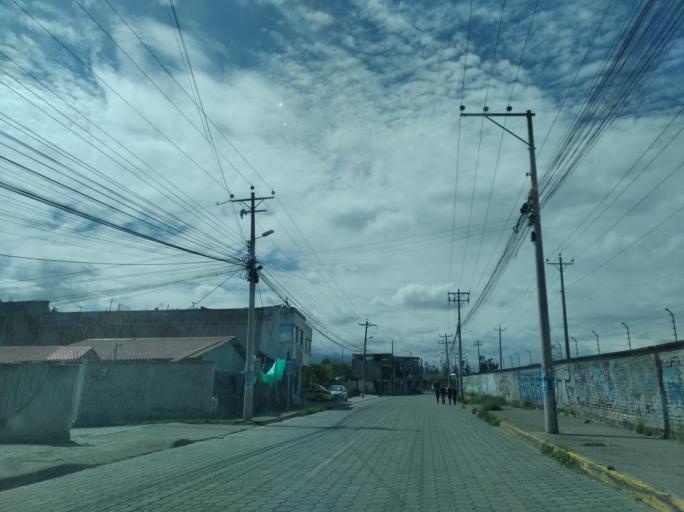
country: EC
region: Pichincha
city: Sangolqui
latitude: -0.2156
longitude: -78.3398
